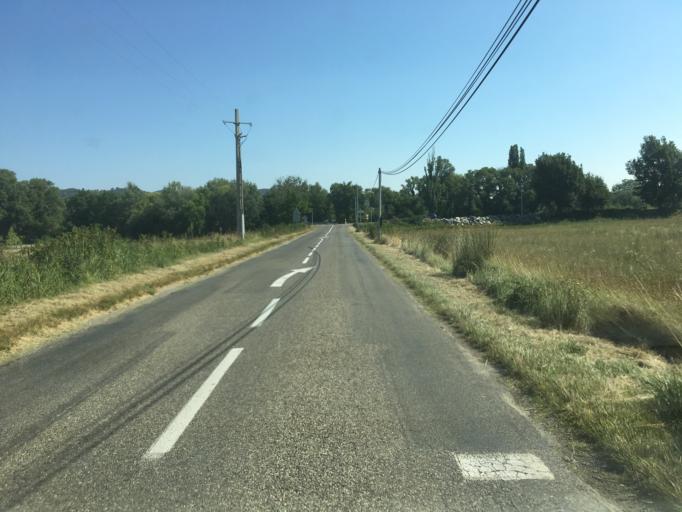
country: FR
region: Provence-Alpes-Cote d'Azur
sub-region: Departement des Alpes-de-Haute-Provence
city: Oraison
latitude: 43.8765
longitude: 5.9079
